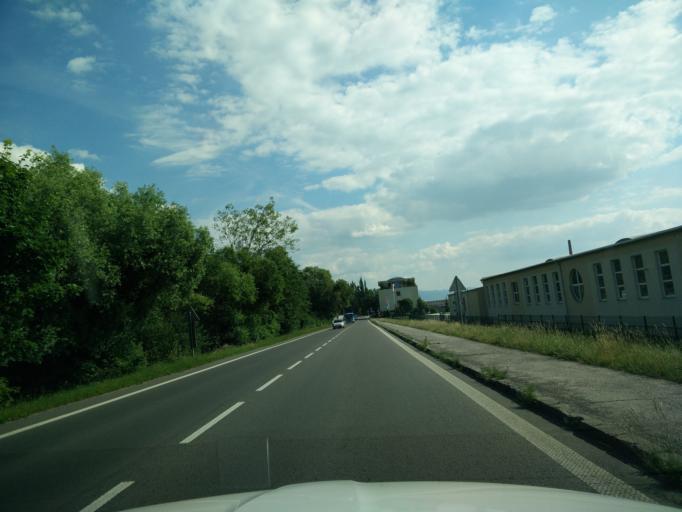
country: SK
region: Nitriansky
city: Prievidza
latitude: 48.8437
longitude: 18.6445
